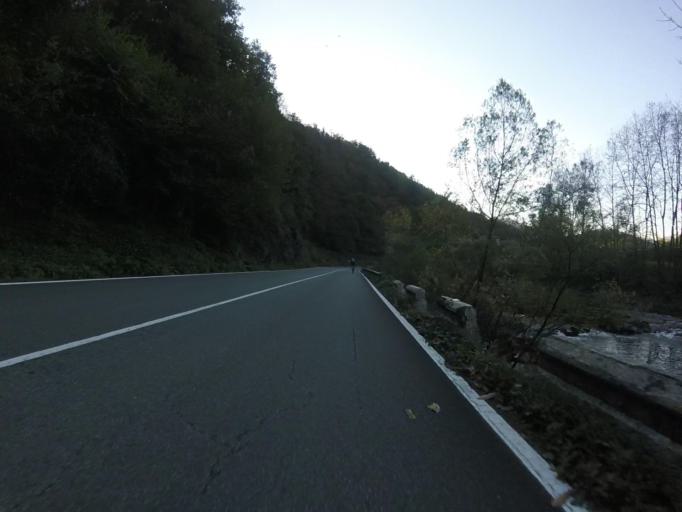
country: ES
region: Navarre
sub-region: Provincia de Navarra
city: Lesaka
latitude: 43.2468
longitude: -1.6693
